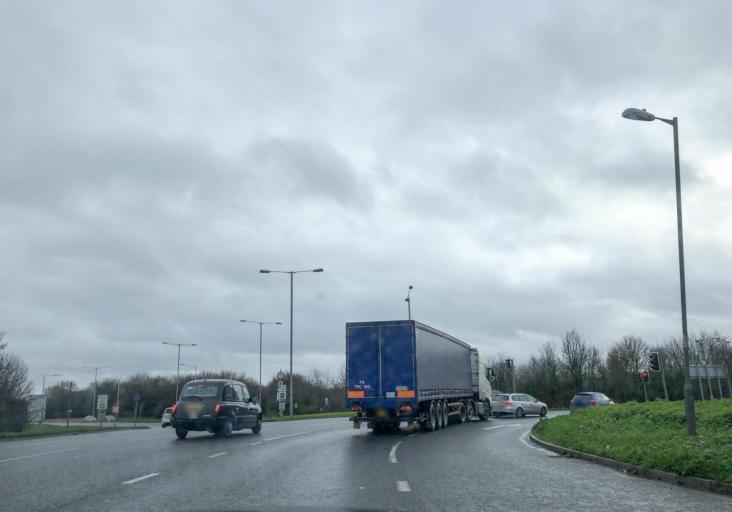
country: GB
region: England
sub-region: Surrey
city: Colnbrook
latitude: 51.4639
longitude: -0.4930
